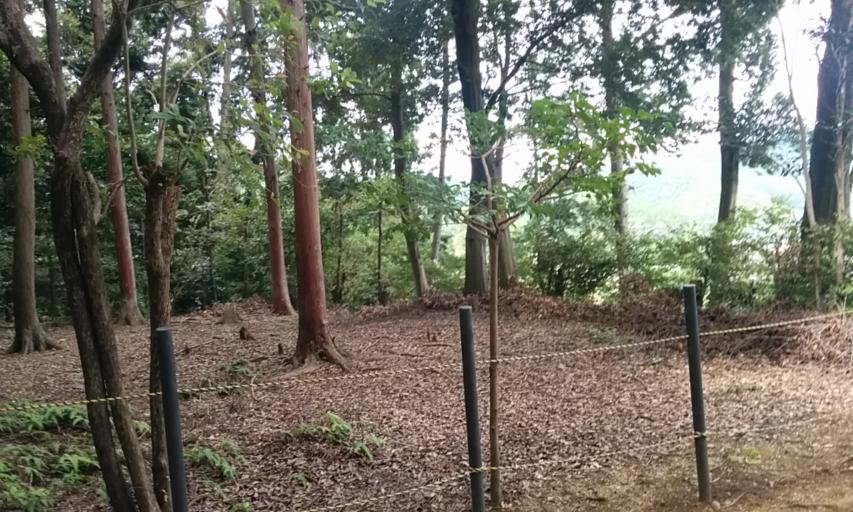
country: JP
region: Kyoto
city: Muko
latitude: 35.0208
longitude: 135.6675
